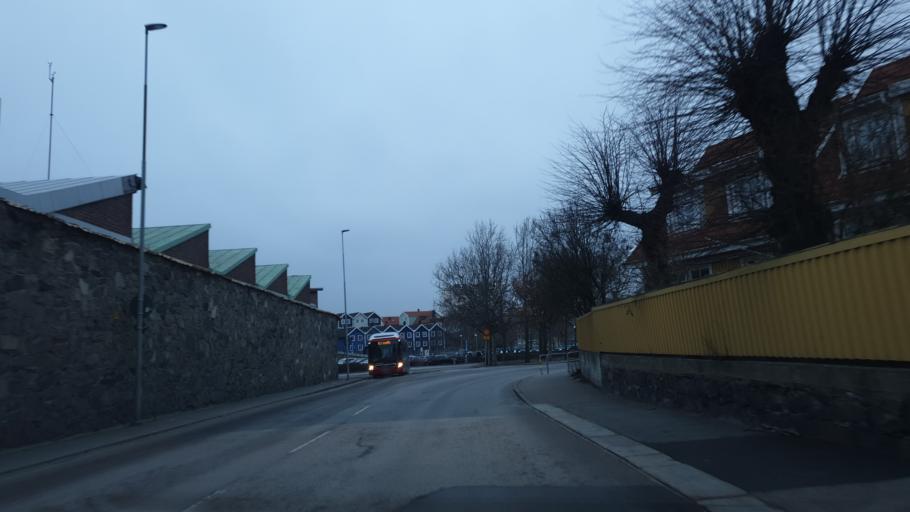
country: SE
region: Blekinge
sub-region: Karlskrona Kommun
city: Karlskrona
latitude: 56.1608
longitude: 15.5771
